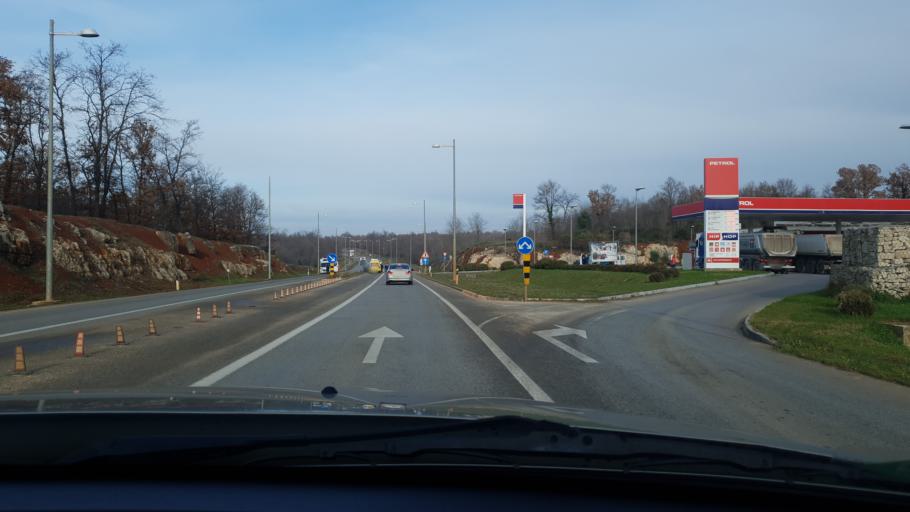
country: HR
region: Istarska
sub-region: Grad Porec
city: Porec
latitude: 45.2391
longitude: 13.6237
